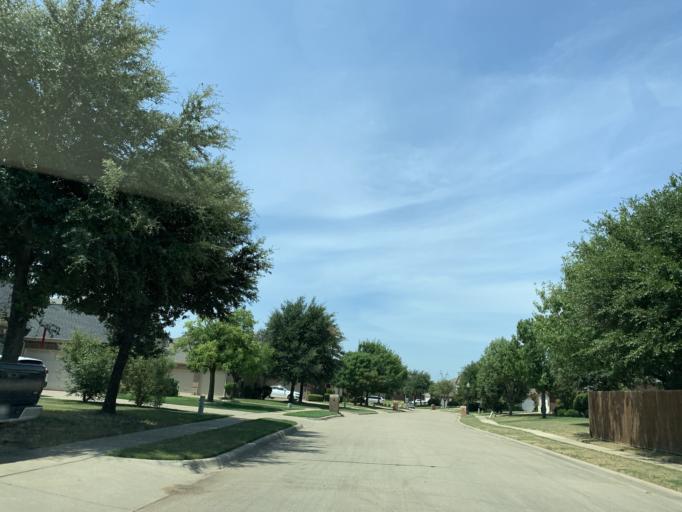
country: US
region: Texas
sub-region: Dallas County
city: Cedar Hill
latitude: 32.6432
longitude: -97.0438
